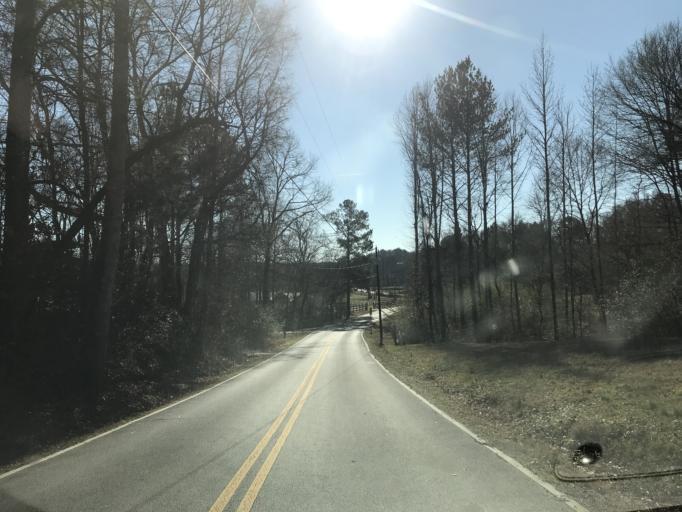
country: US
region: Georgia
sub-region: Paulding County
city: Dallas
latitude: 34.0008
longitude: -84.8975
